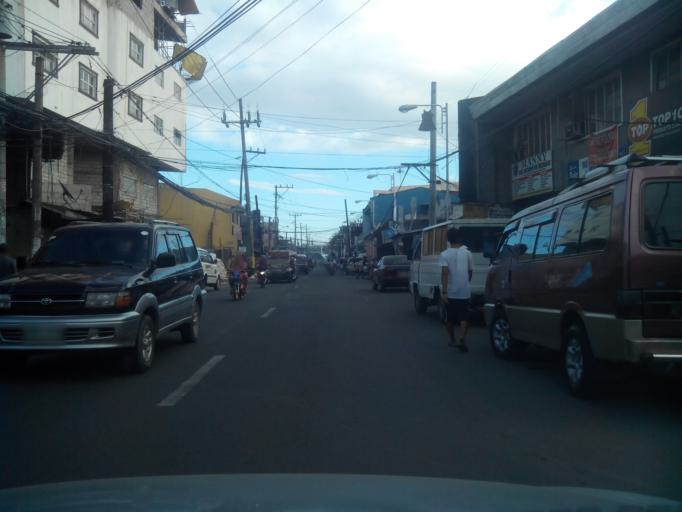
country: PH
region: Calabarzon
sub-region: Province of Rizal
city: Taytay
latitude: 14.5651
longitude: 121.1323
